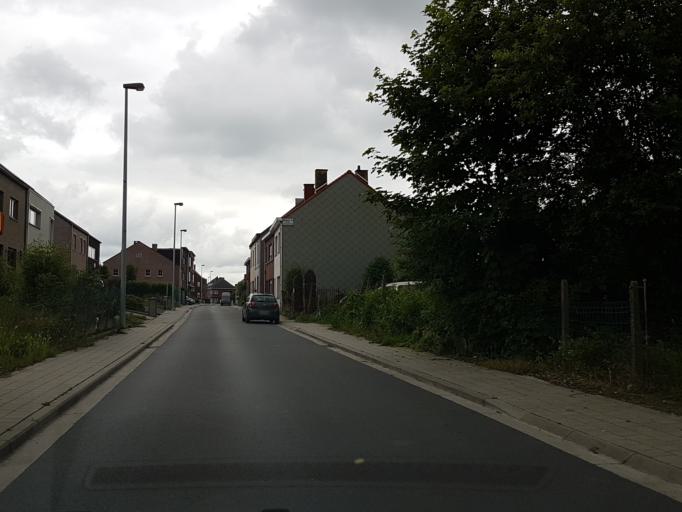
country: BE
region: Flanders
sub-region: Provincie Oost-Vlaanderen
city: Denderleeuw
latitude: 50.9090
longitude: 4.0771
